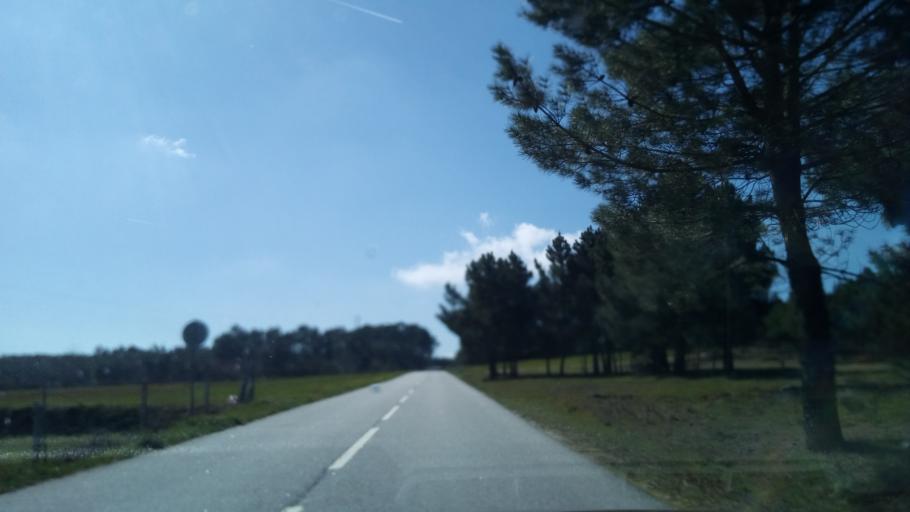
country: PT
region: Guarda
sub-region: Fornos de Algodres
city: Fornos de Algodres
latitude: 40.6437
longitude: -7.5316
